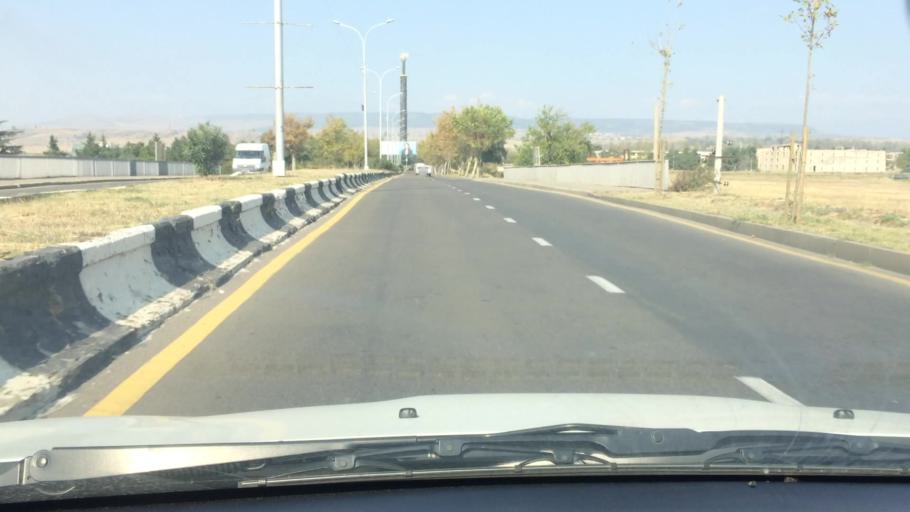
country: GE
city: Didi Lilo
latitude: 41.6864
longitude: 44.9533
